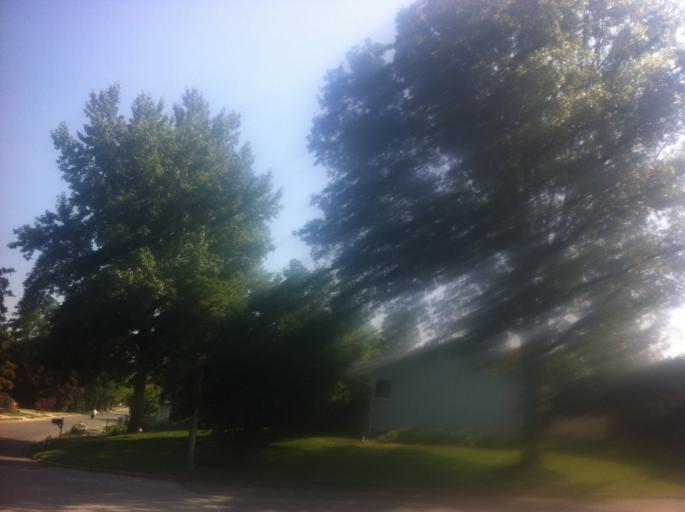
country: US
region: New York
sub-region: Nassau County
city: Locust Valley
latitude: 40.8584
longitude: -73.6023
